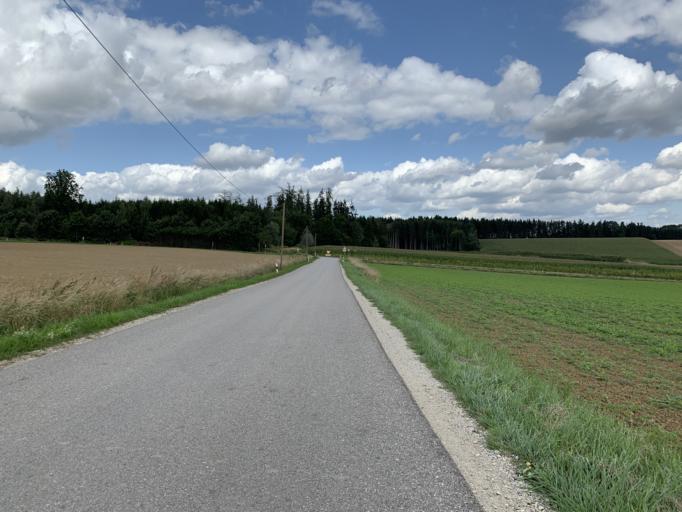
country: DE
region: Bavaria
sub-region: Upper Bavaria
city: Zolling
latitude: 48.4291
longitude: 11.7681
